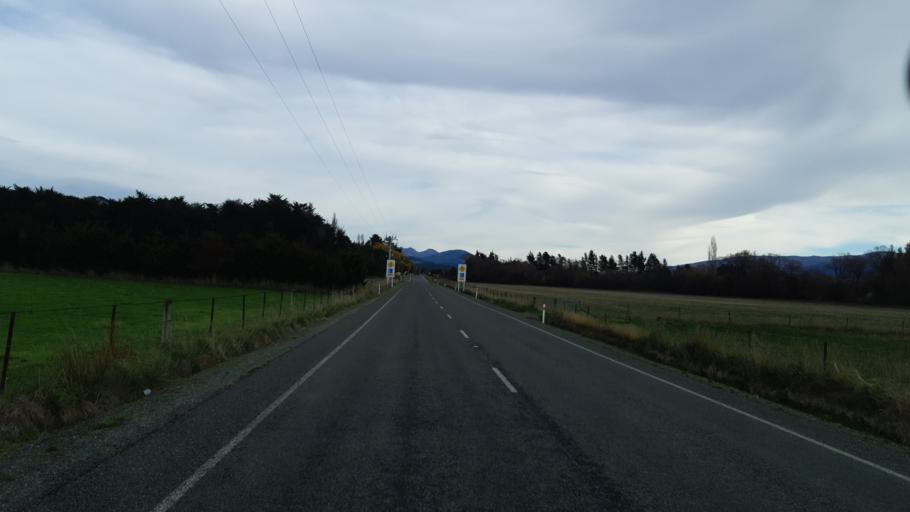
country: NZ
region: Tasman
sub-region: Tasman District
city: Brightwater
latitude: -41.6322
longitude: 173.3293
